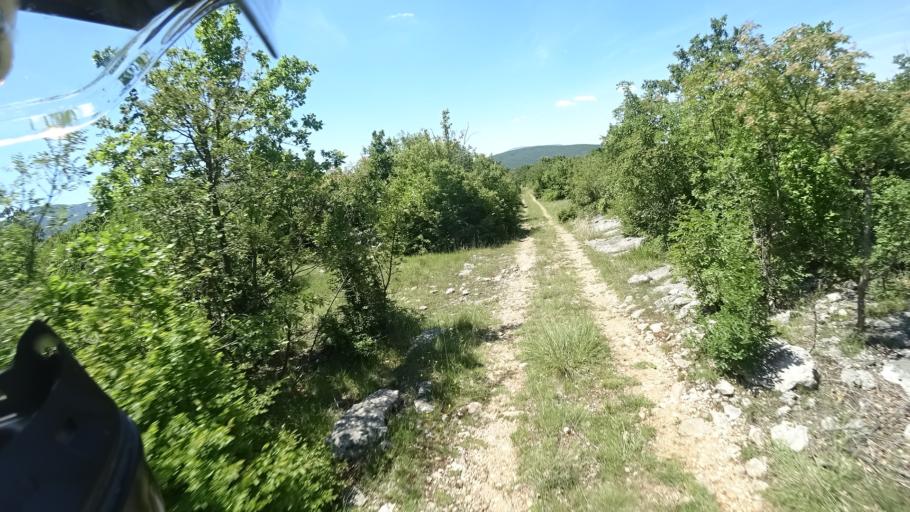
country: HR
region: Sibensko-Kniniska
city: Knin
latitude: 44.0077
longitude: 16.3132
